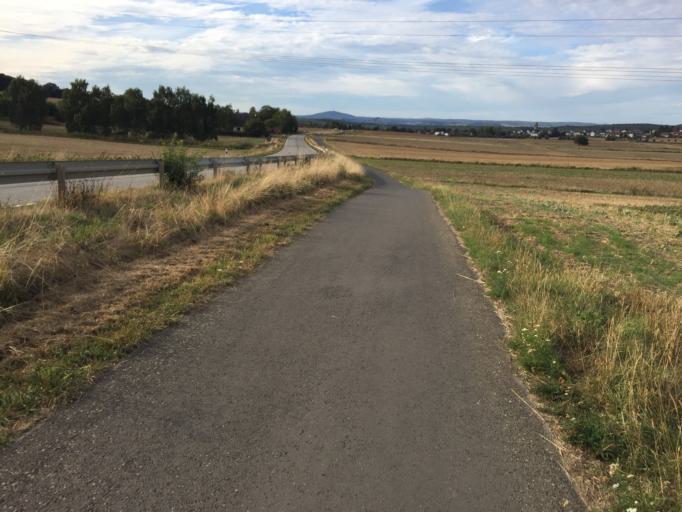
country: DE
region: Hesse
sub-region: Regierungsbezirk Giessen
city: Langgons
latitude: 50.5216
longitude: 8.7212
